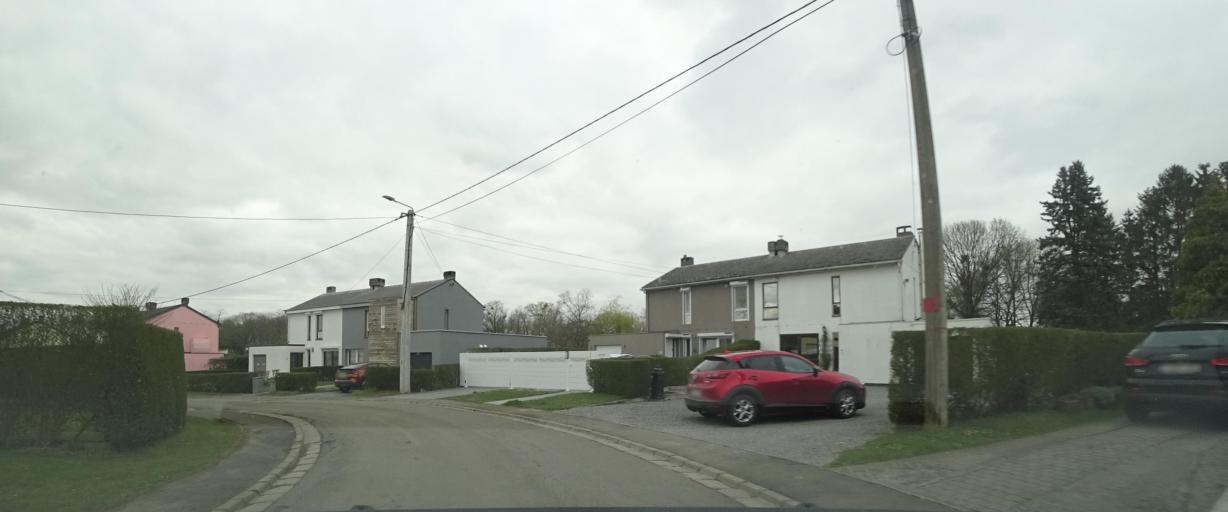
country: BE
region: Wallonia
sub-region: Province du Luxembourg
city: Marche-en-Famenne
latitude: 50.2244
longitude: 5.3519
